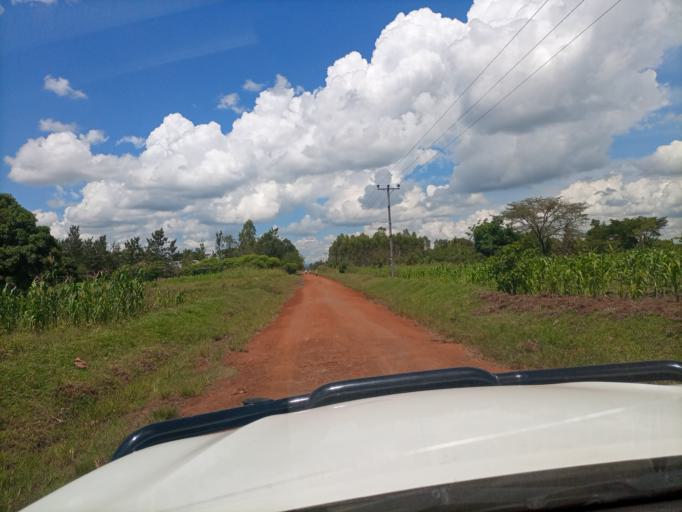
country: UG
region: Eastern Region
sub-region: Tororo District
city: Tororo
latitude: 0.6673
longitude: 34.0027
